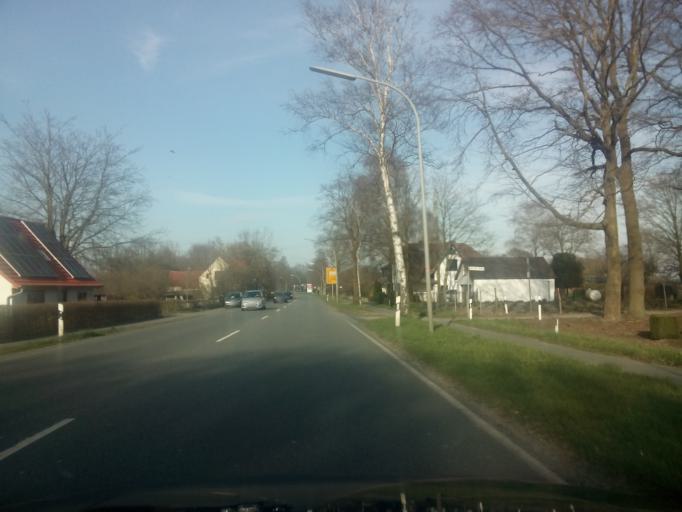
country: DE
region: Lower Saxony
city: Osterholz-Scharmbeck
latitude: 53.2118
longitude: 8.7715
